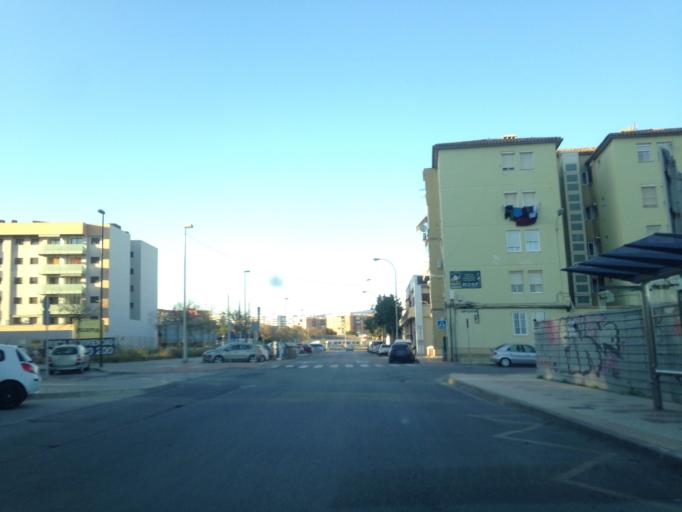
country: ES
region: Andalusia
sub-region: Provincia de Malaga
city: Malaga
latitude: 36.6864
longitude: -4.4480
